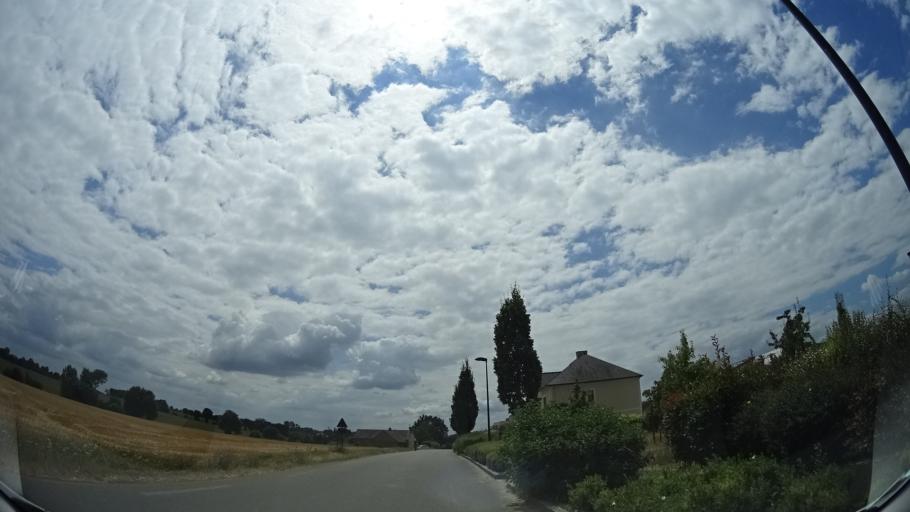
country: FR
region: Brittany
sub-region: Departement d'Ille-et-Vilaine
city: Pace
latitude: 48.1629
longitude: -1.7616
